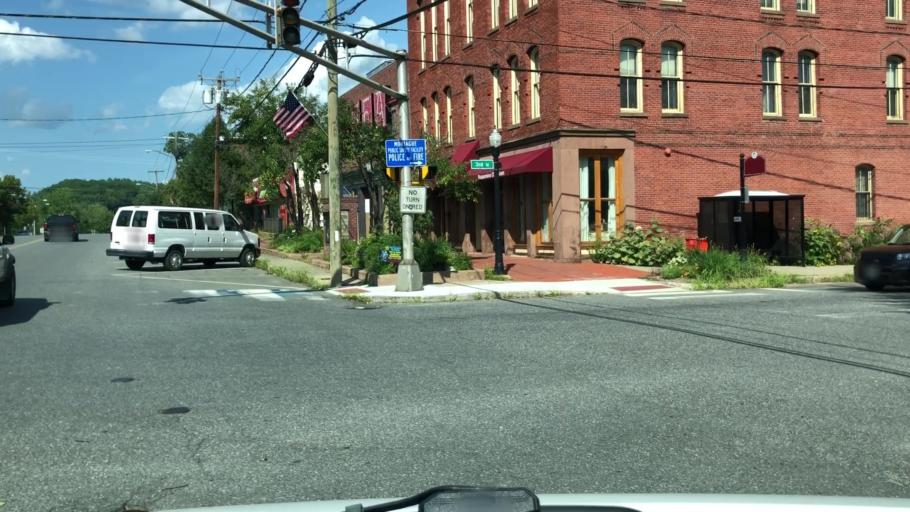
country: US
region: Massachusetts
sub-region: Franklin County
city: Turners Falls
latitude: 42.6081
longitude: -72.5569
